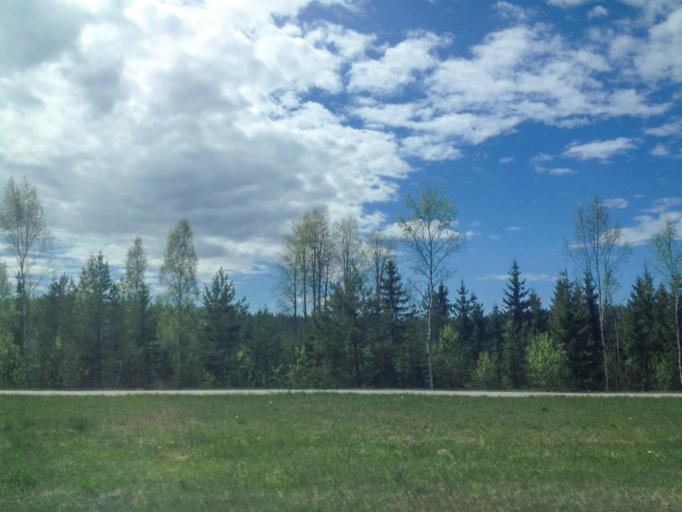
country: FI
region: Haeme
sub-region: Riihimaeki
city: Riihimaeki
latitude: 60.6726
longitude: 24.7750
